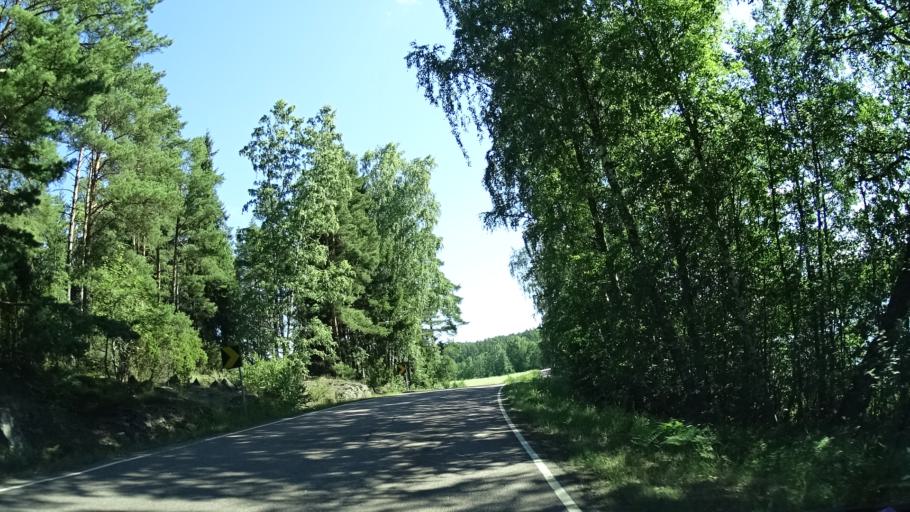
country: FI
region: Varsinais-Suomi
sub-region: Turku
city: Merimasku
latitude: 60.5155
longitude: 21.8147
